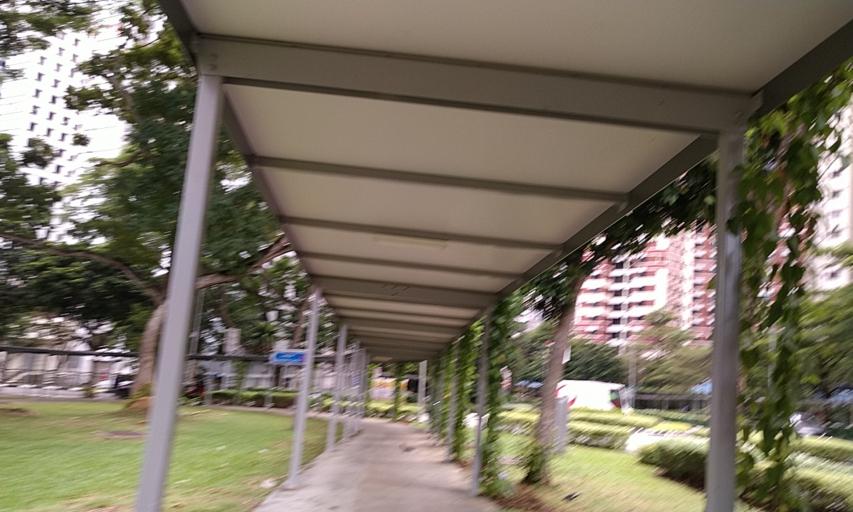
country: SG
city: Singapore
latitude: 1.2883
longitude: 103.8148
